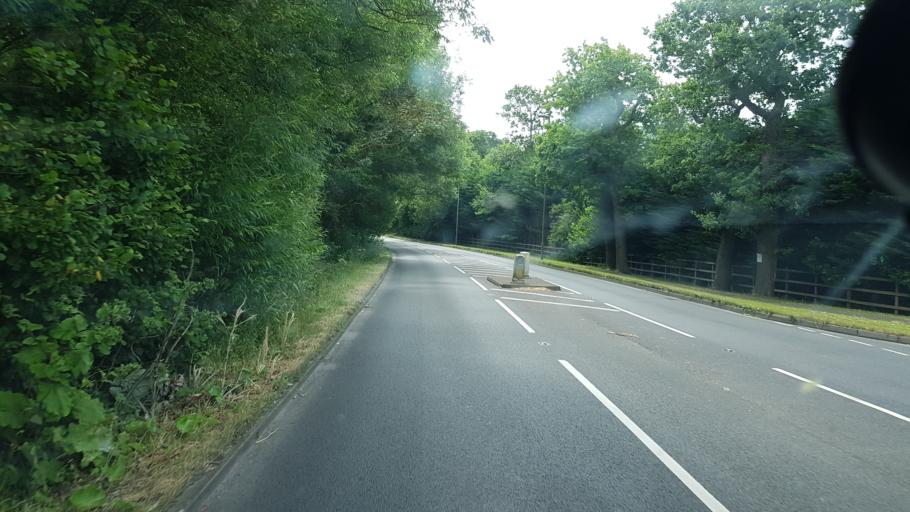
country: GB
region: England
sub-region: Surrey
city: Felbridge
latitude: 51.1553
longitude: -0.0501
